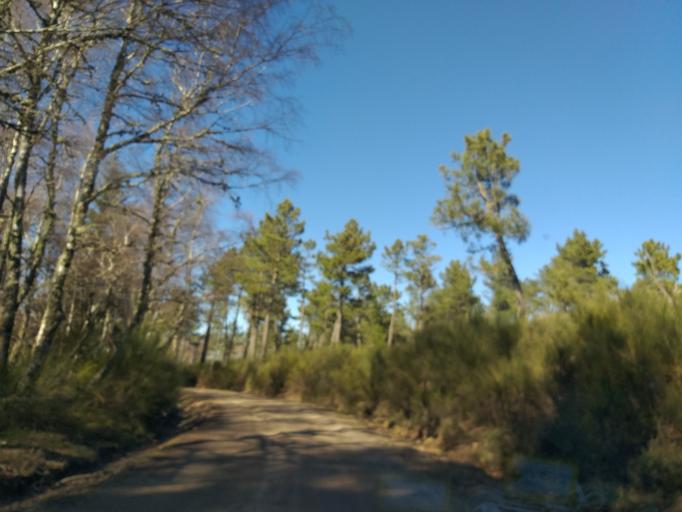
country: PT
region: Guarda
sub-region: Manteigas
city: Manteigas
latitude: 40.4893
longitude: -7.4917
